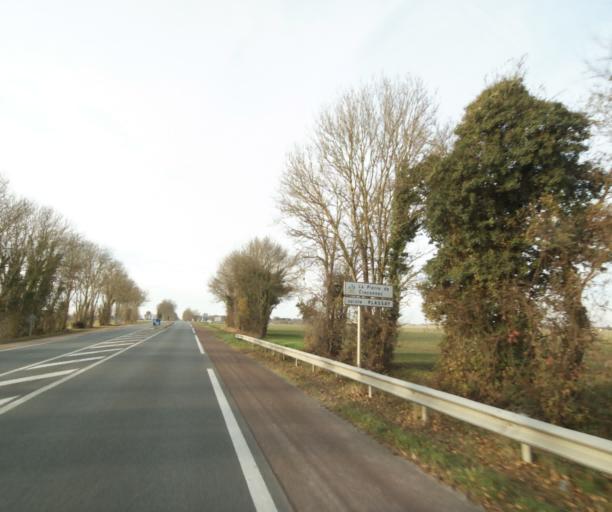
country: FR
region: Poitou-Charentes
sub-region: Departement de la Charente-Maritime
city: Nieul-les-Saintes
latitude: 45.7992
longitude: -0.7419
